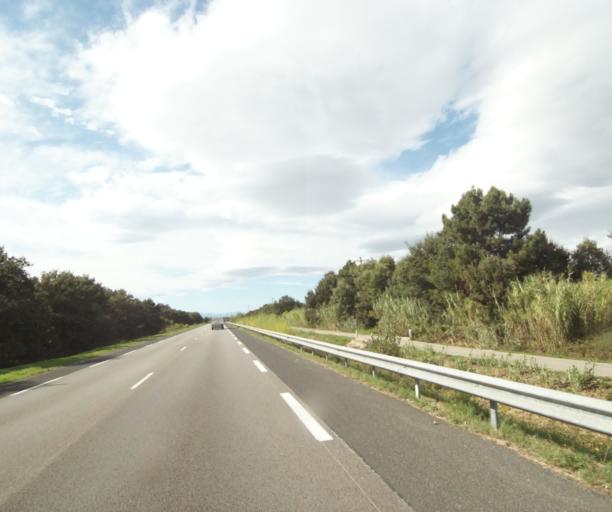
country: FR
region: Languedoc-Roussillon
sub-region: Departement des Pyrenees-Orientales
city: Sant Andreu de Sureda
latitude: 42.5554
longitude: 2.9852
